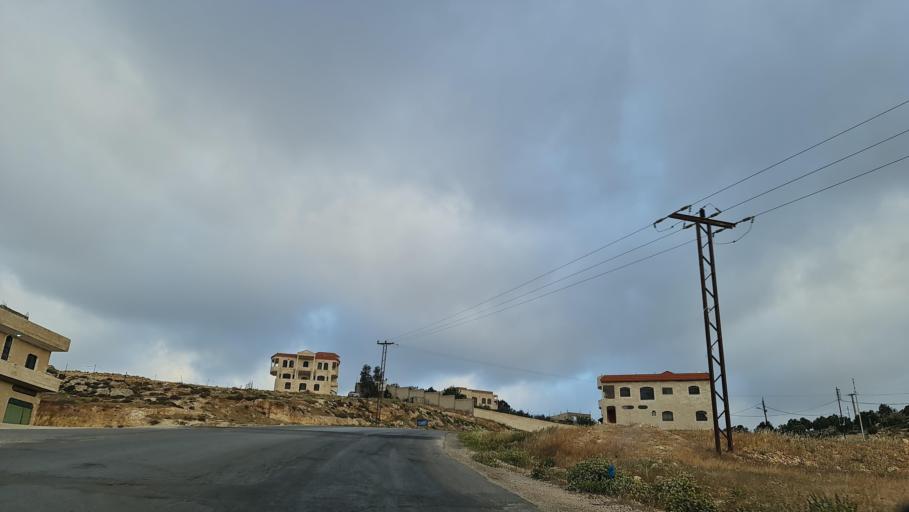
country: JO
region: Amman
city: Al Jubayhah
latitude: 32.0934
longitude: 35.9036
